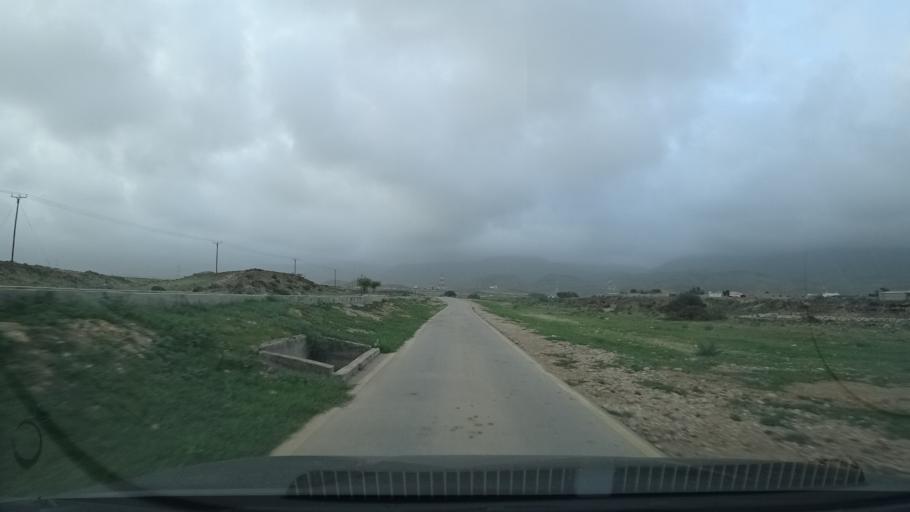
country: OM
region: Zufar
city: Salalah
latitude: 17.0943
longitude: 54.2333
